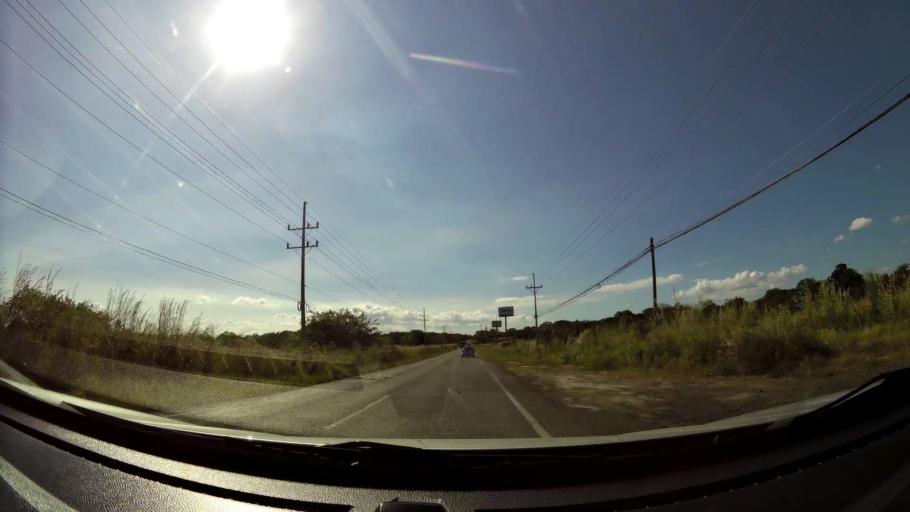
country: CR
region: Guanacaste
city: Liberia
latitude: 10.6144
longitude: -85.4807
